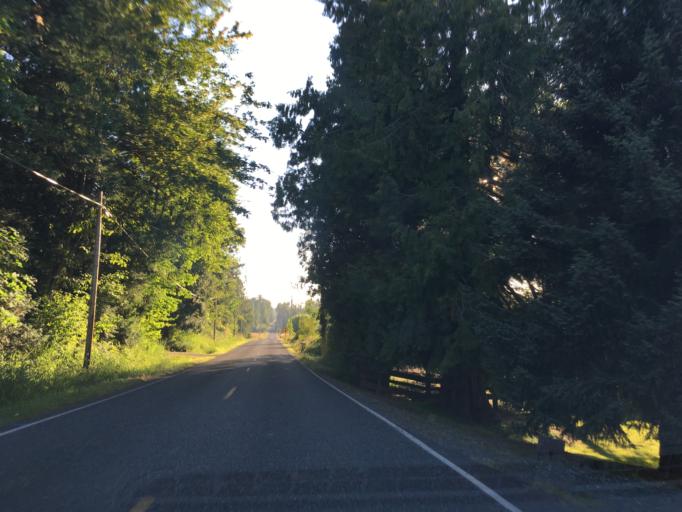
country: US
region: Washington
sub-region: Whatcom County
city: Sudden Valley
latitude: 48.8181
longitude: -122.3295
